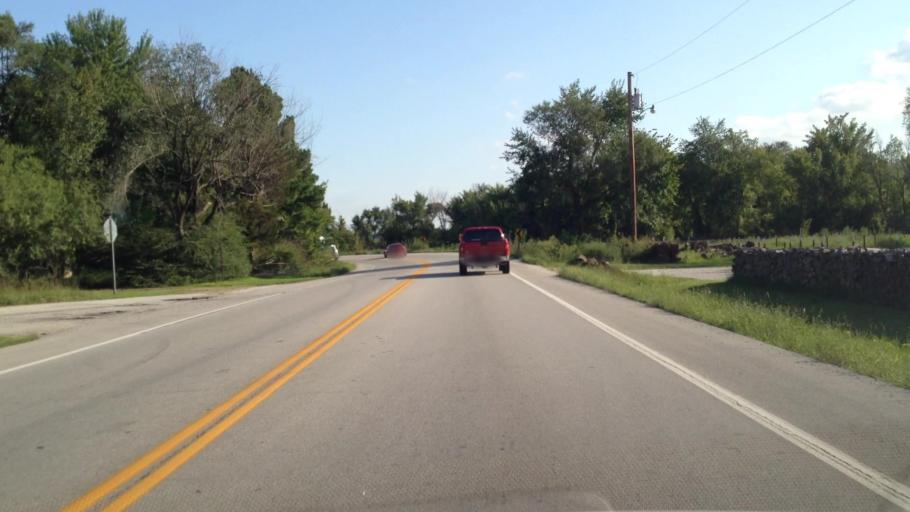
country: US
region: Missouri
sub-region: Jasper County
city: Carl Junction
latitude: 37.2737
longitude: -94.6011
